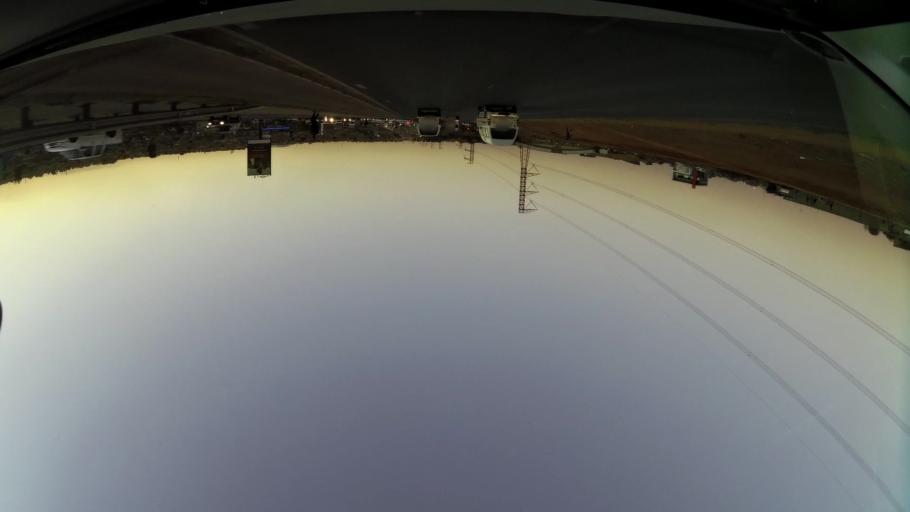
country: ZA
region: Gauteng
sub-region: Ekurhuleni Metropolitan Municipality
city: Tembisa
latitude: -26.0332
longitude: 28.1924
